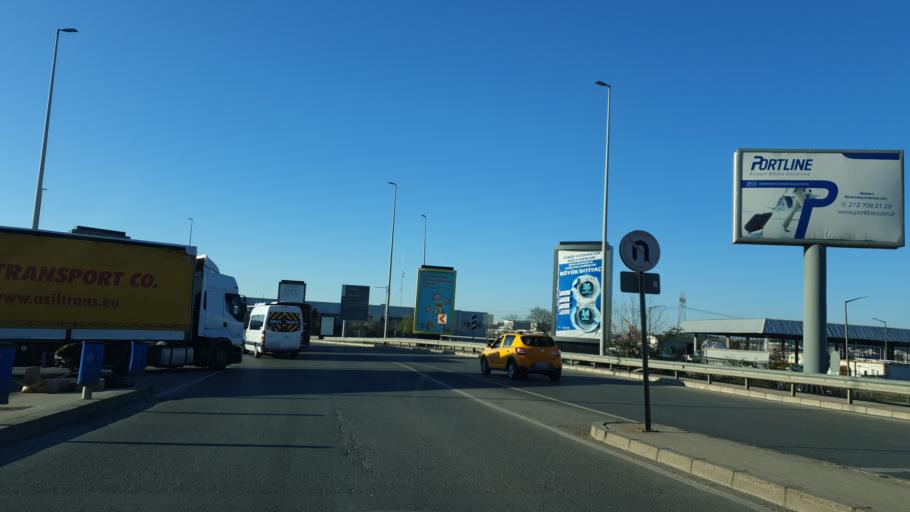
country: TR
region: Istanbul
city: Pendik
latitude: 40.9101
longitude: 29.3168
